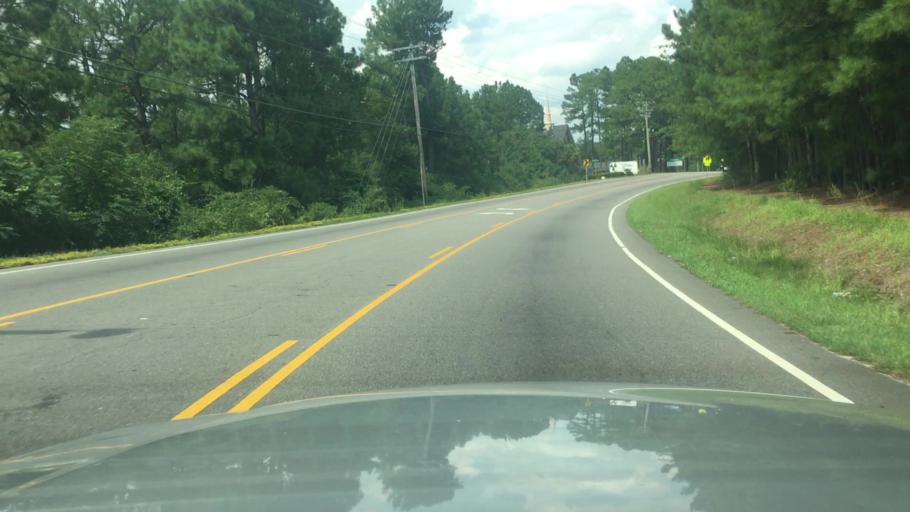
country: US
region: North Carolina
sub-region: Cumberland County
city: Spring Lake
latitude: 35.1201
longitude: -78.9137
